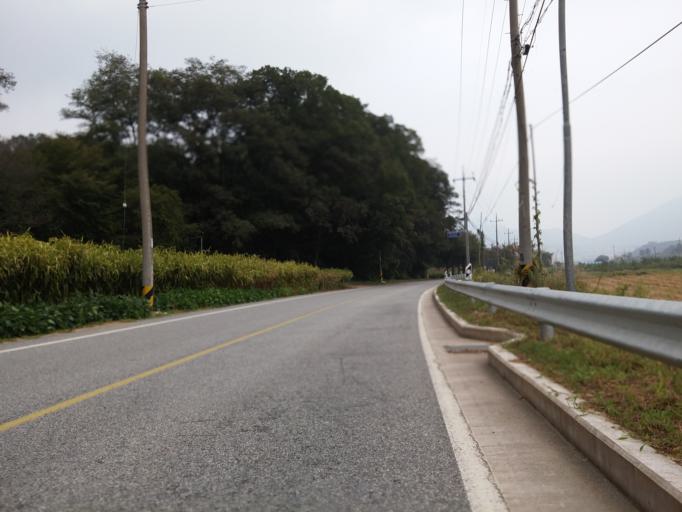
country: KR
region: Chungcheongbuk-do
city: Okcheon
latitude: 36.3928
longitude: 127.7084
